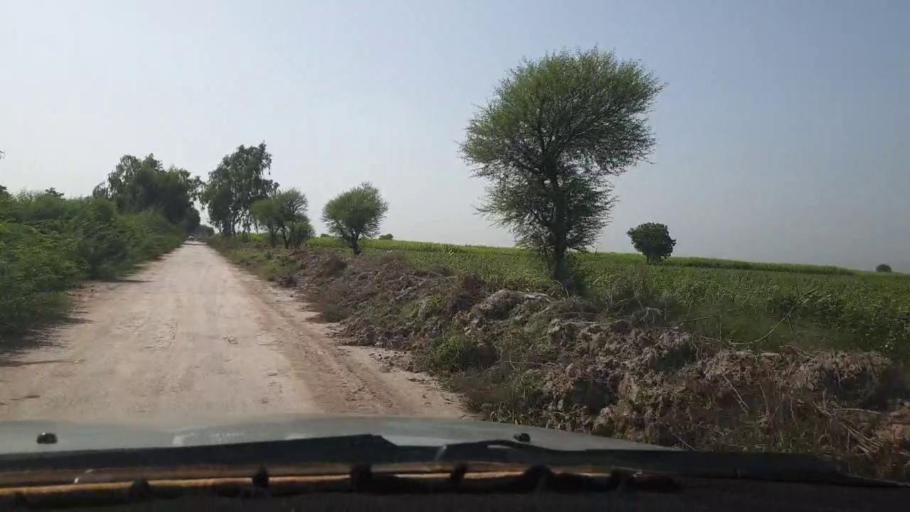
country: PK
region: Sindh
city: Chambar
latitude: 25.2446
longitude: 68.9166
